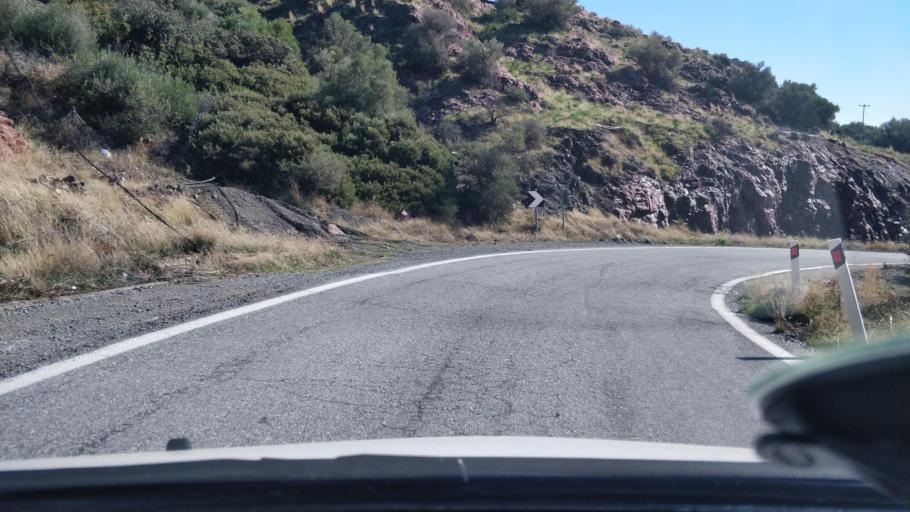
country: GR
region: Crete
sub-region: Nomos Irakleiou
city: Arkalochori
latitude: 35.0061
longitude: 25.4347
